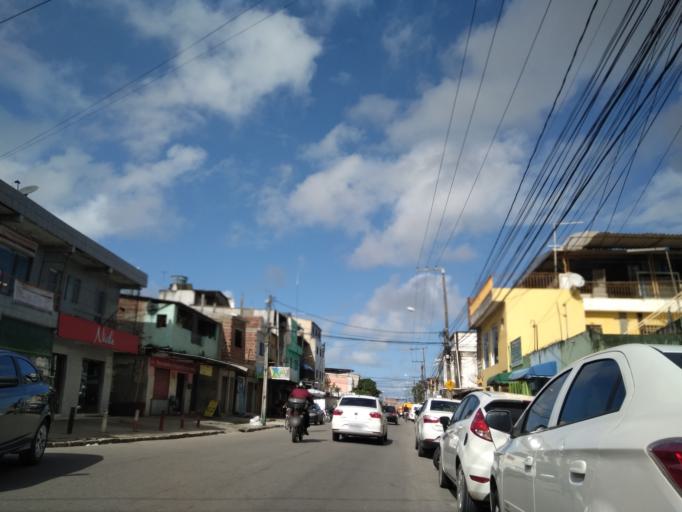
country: BR
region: Pernambuco
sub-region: Recife
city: Recife
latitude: -8.0713
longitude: -34.9280
